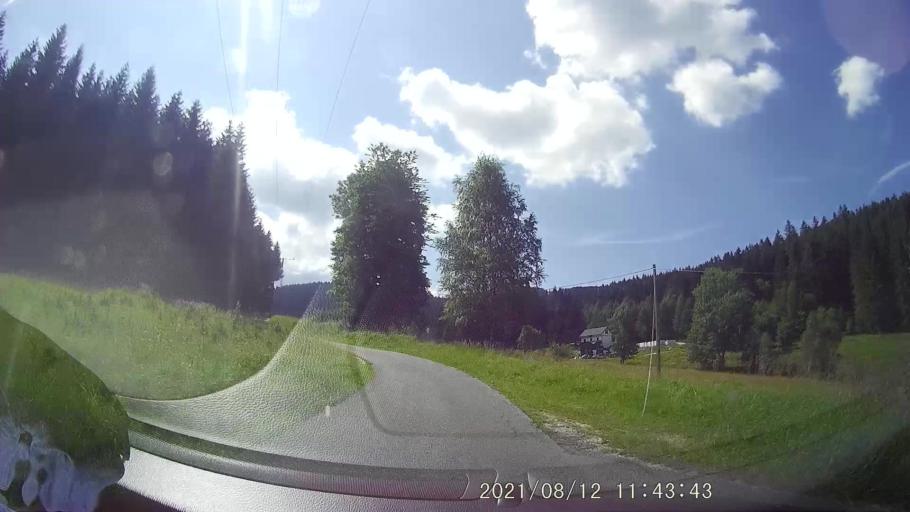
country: PL
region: Lower Silesian Voivodeship
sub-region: Powiat klodzki
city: Stronie Slaskie
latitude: 50.2608
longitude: 16.8340
